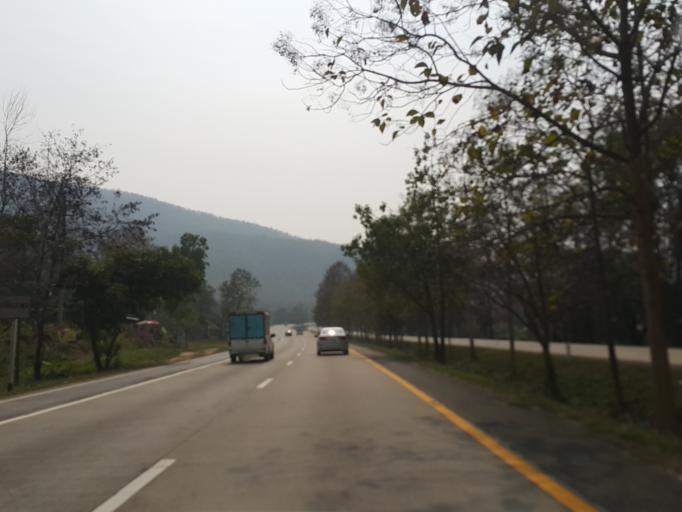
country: TH
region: Lamphun
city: Mae Tha
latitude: 18.5028
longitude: 99.1328
